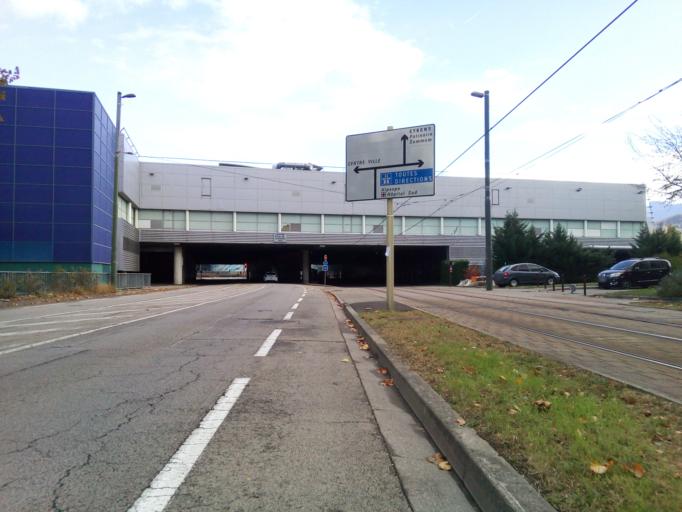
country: FR
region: Rhone-Alpes
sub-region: Departement de l'Isere
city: Echirolles
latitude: 45.1573
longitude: 5.7313
